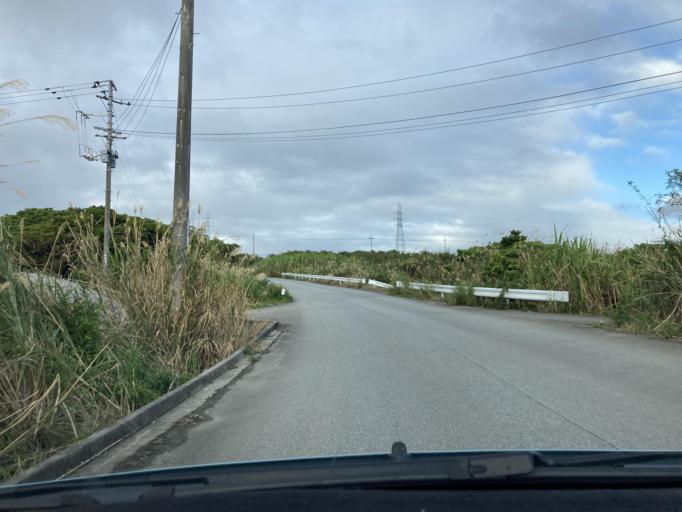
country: JP
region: Okinawa
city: Itoman
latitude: 26.1181
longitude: 127.6847
